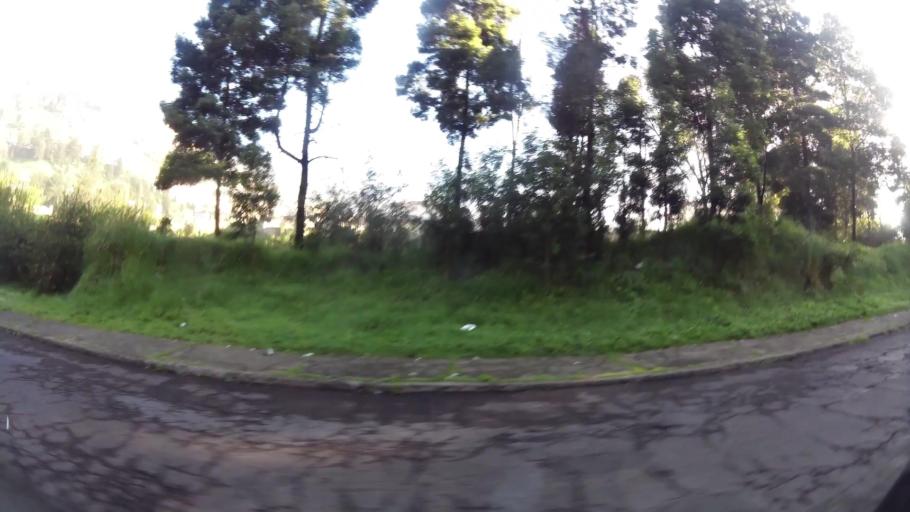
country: EC
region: Pichincha
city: Quito
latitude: -0.2341
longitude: -78.5121
